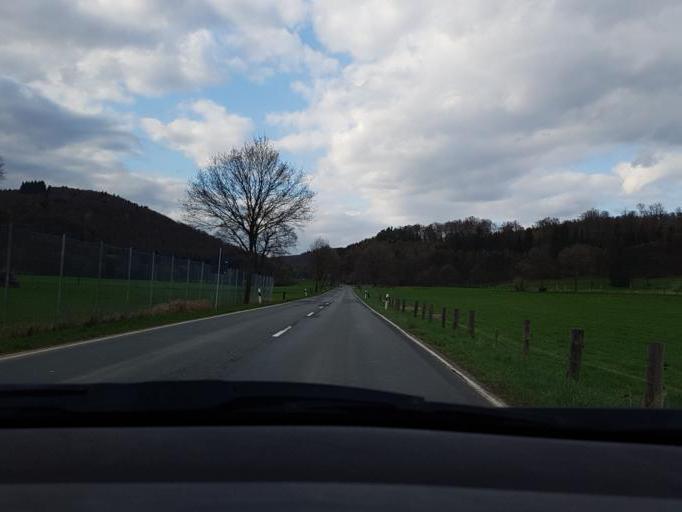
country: DE
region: Lower Saxony
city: Bodenfelde
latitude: 51.6525
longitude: 9.5482
